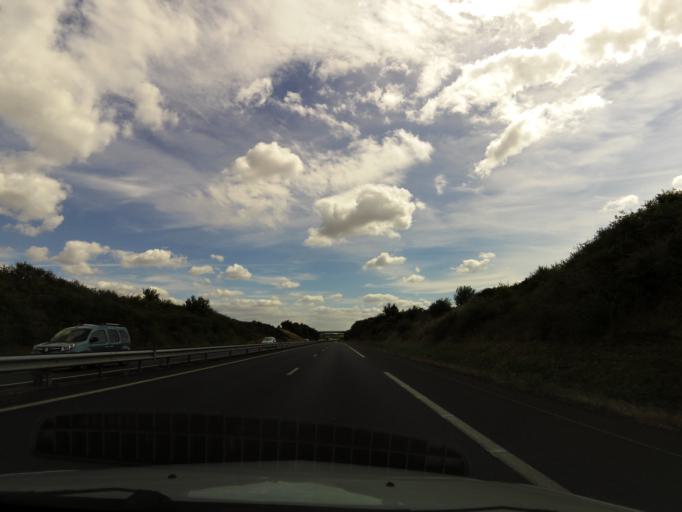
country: FR
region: Pays de la Loire
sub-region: Departement de la Vendee
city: Les Brouzils
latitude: 46.9212
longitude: -1.3307
